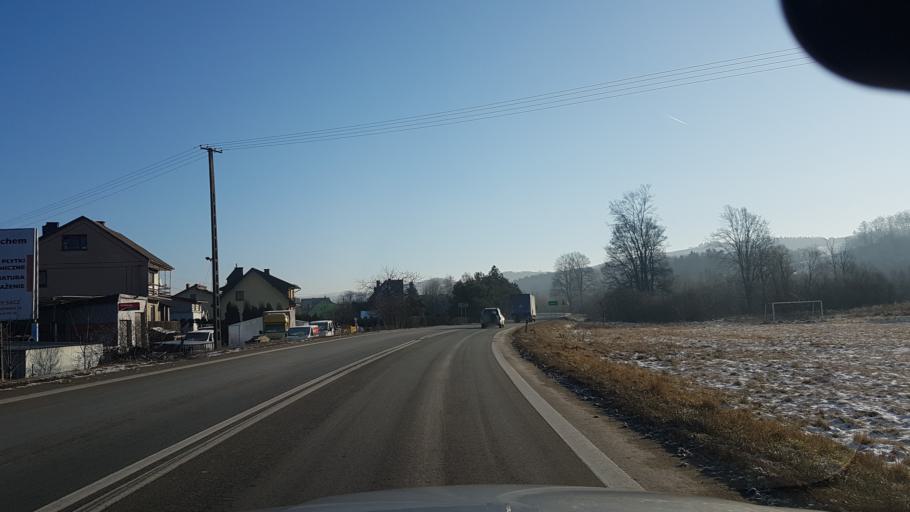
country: PL
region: Lesser Poland Voivodeship
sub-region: Powiat nowosadecki
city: Olszana
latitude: 49.5344
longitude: 20.5321
